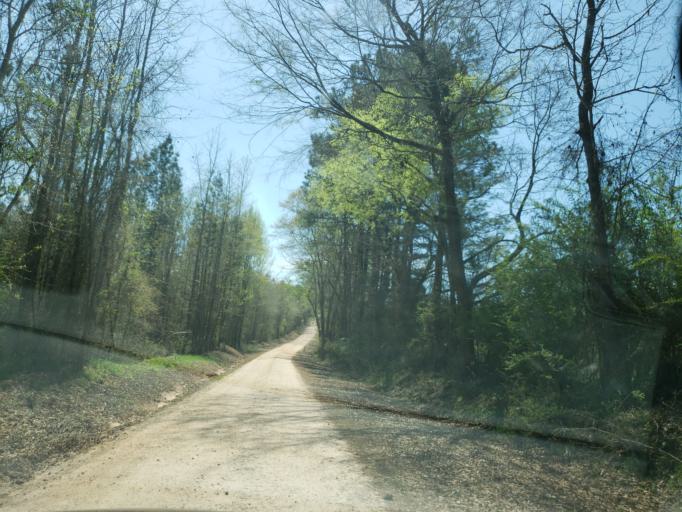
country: US
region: Alabama
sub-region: Tallapoosa County
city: Camp Hill
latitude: 32.6645
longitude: -85.6623
